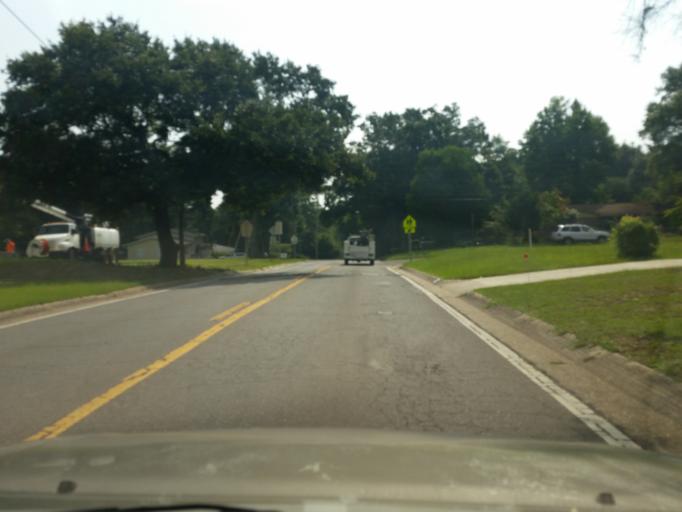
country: US
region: Florida
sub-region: Escambia County
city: Goulding
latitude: 30.4498
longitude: -87.2059
